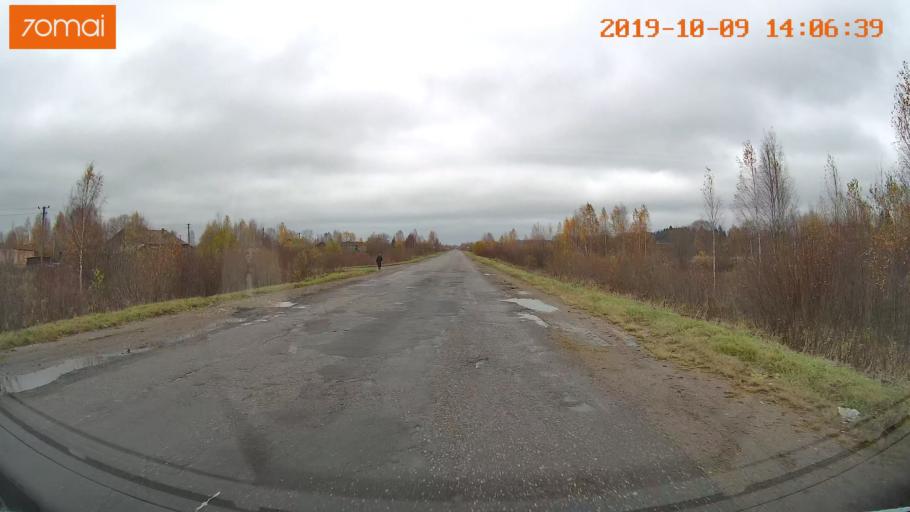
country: RU
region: Kostroma
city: Buy
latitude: 58.4659
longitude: 41.4131
